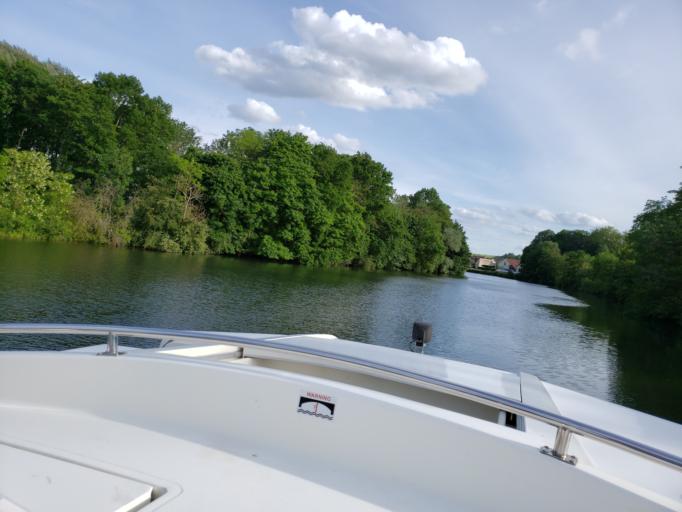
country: FR
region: Bourgogne
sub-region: Departement de l'Yonne
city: Cheny
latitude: 47.9315
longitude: 3.5162
